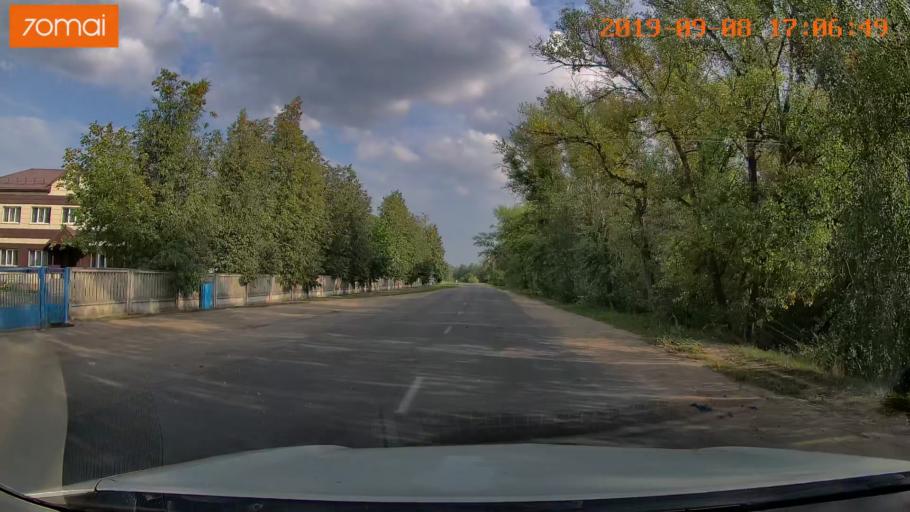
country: BY
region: Grodnenskaya
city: Hrodna
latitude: 53.6676
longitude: 23.9530
